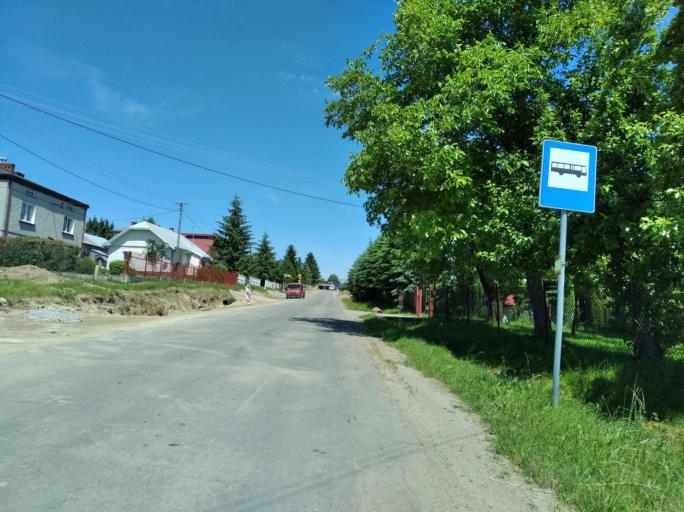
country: PL
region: Subcarpathian Voivodeship
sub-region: Powiat jasielski
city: Tarnowiec
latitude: 49.7086
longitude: 21.5534
